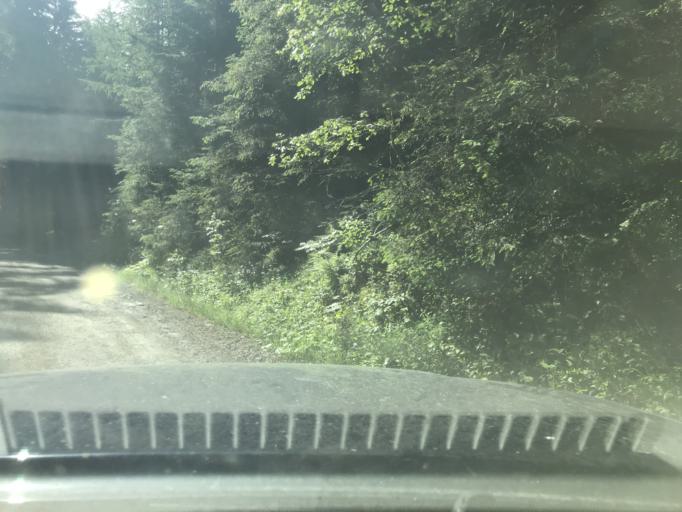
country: AT
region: Styria
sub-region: Politischer Bezirk Murau
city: Sankt Peter am Kammersberg
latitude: 47.2165
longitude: 14.1760
